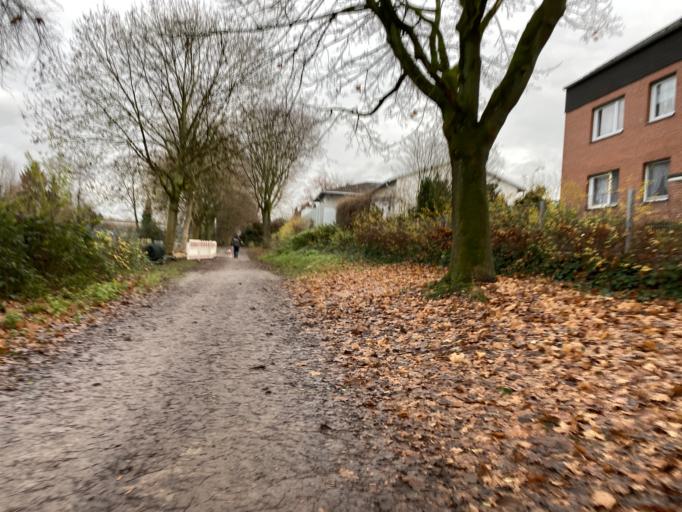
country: DE
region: North Rhine-Westphalia
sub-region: Regierungsbezirk Arnsberg
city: Hamm
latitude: 51.6771
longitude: 7.8424
